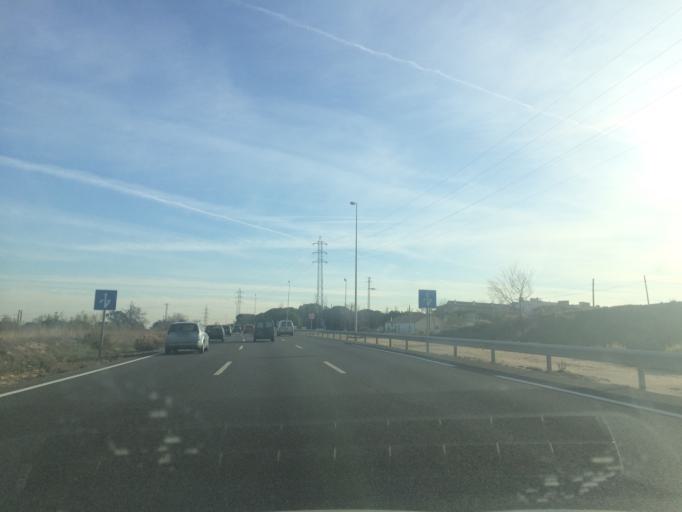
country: ES
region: Madrid
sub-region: Provincia de Madrid
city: Las Tablas
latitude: 40.5422
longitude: -3.7017
